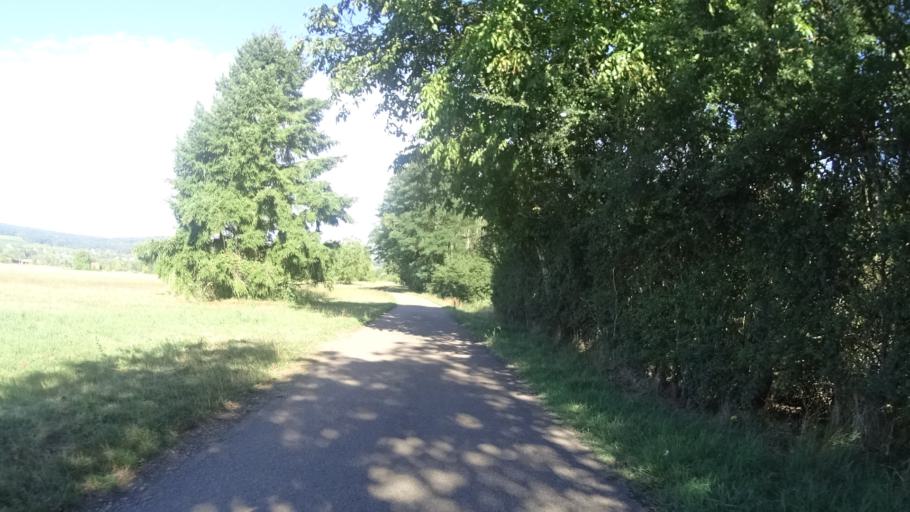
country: FR
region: Centre
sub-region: Departement du Cher
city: Sancerre
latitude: 47.3155
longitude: 2.8763
